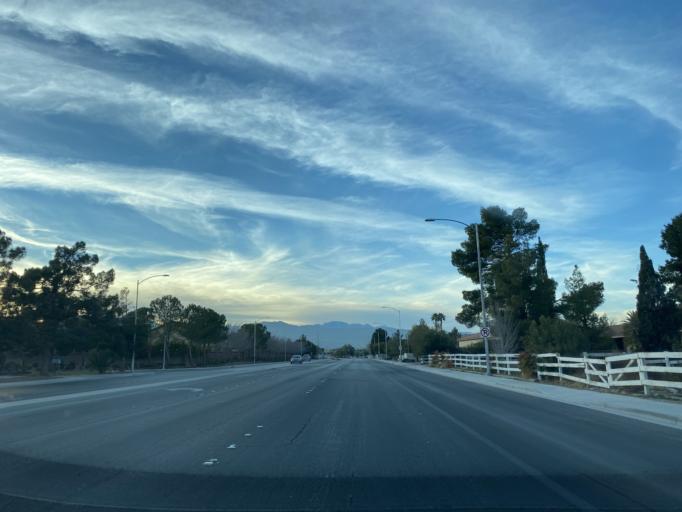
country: US
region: Nevada
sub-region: Clark County
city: Las Vegas
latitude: 36.2626
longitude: -115.2374
